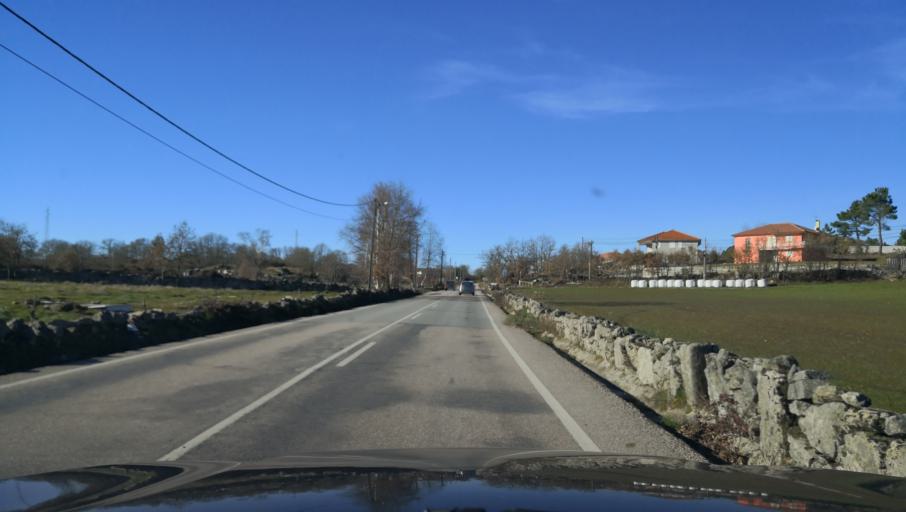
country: PT
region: Vila Real
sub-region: Vila Pouca de Aguiar
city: Vila Pouca de Aguiar
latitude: 41.4975
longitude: -7.6812
